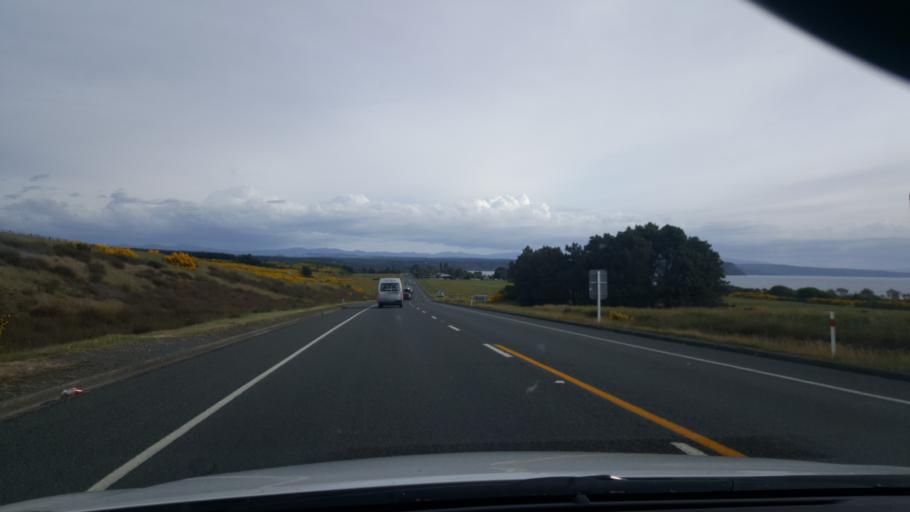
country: NZ
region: Waikato
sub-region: Taupo District
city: Taupo
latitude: -38.7432
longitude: 176.0731
